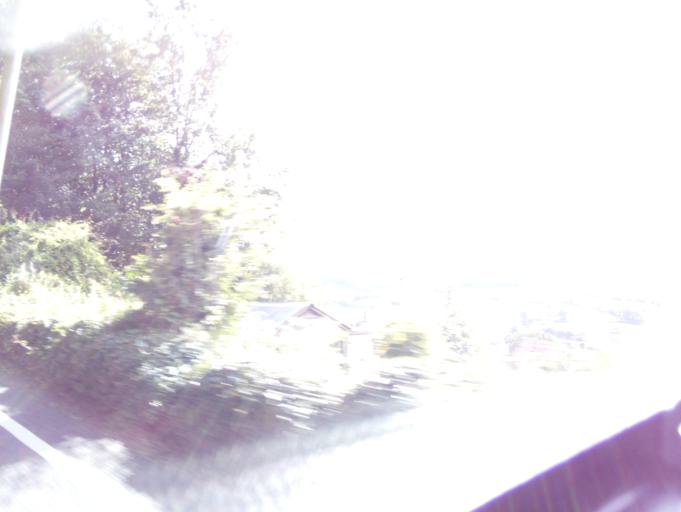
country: GB
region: England
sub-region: Gloucestershire
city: Painswick
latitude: 51.7860
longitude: -2.2234
